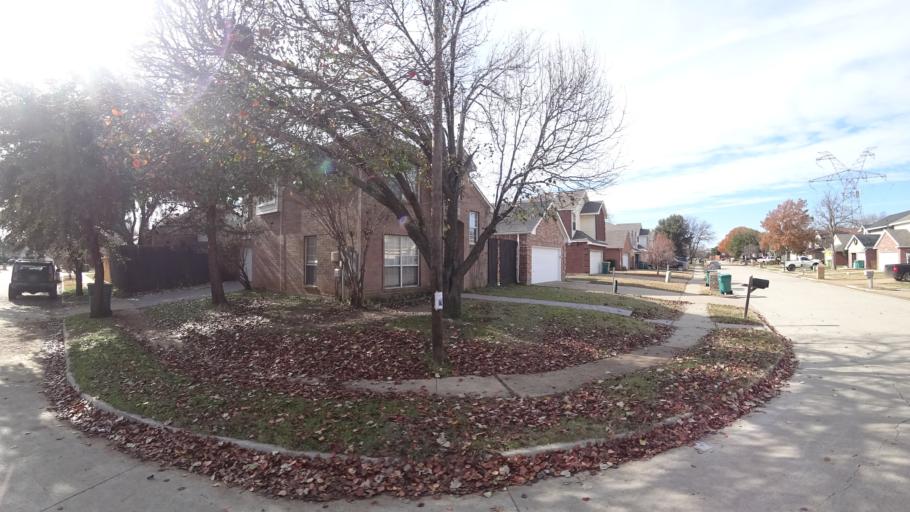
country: US
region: Texas
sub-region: Denton County
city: Highland Village
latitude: 33.0687
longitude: -97.0297
